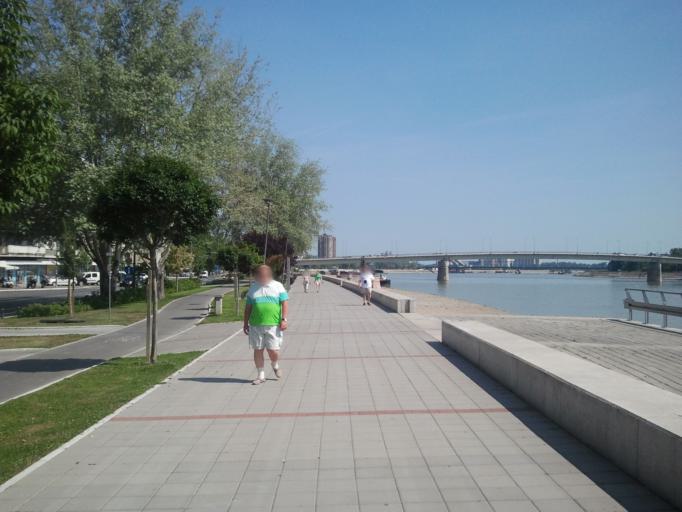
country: RS
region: Autonomna Pokrajina Vojvodina
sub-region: Juznobacki Okrug
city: Novi Sad
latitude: 45.2508
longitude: 19.8559
